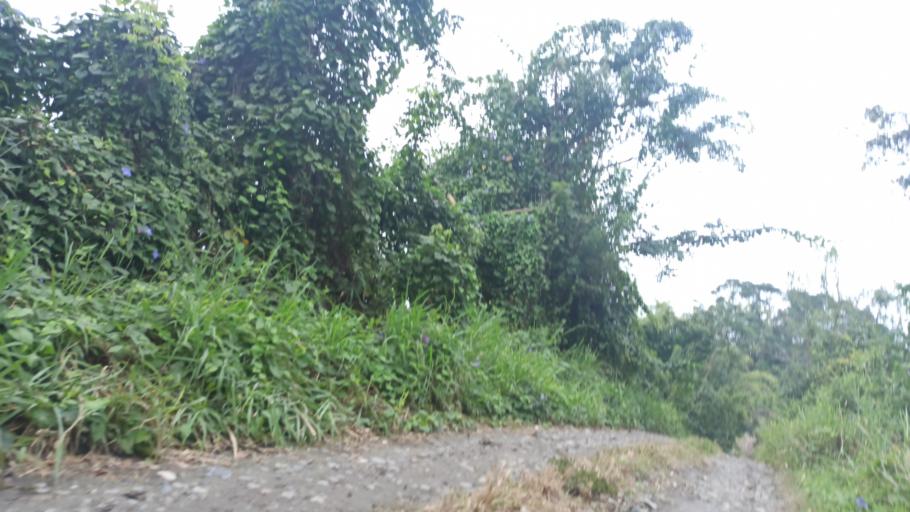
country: MX
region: Puebla
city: Espinal
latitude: 20.2982
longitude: -97.4018
